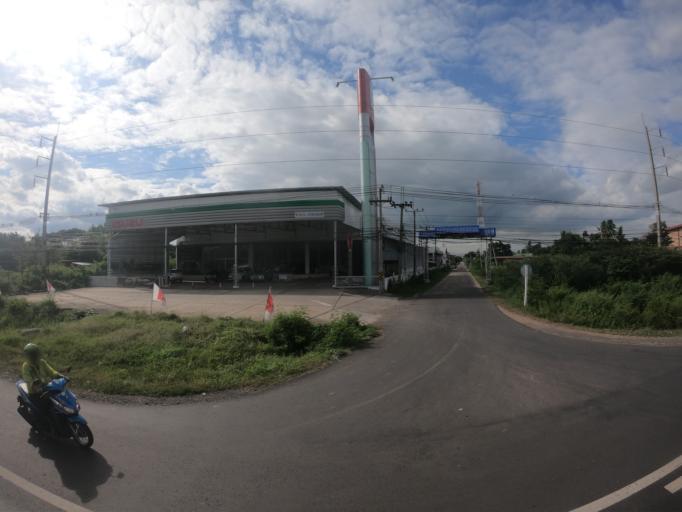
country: TH
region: Surin
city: Prasat
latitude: 14.6296
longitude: 103.4036
